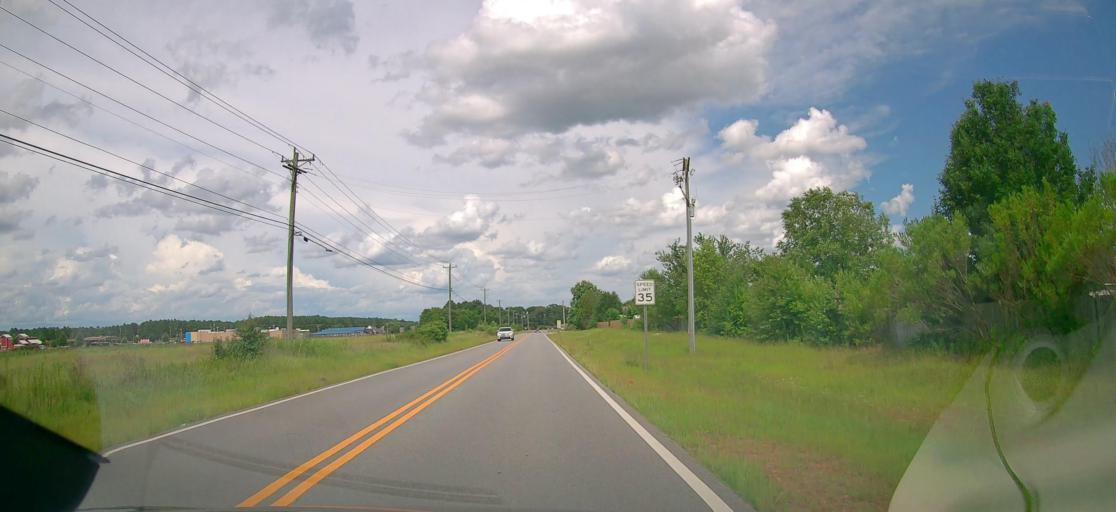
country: US
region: Georgia
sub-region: Houston County
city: Centerville
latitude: 32.5785
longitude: -83.7000
